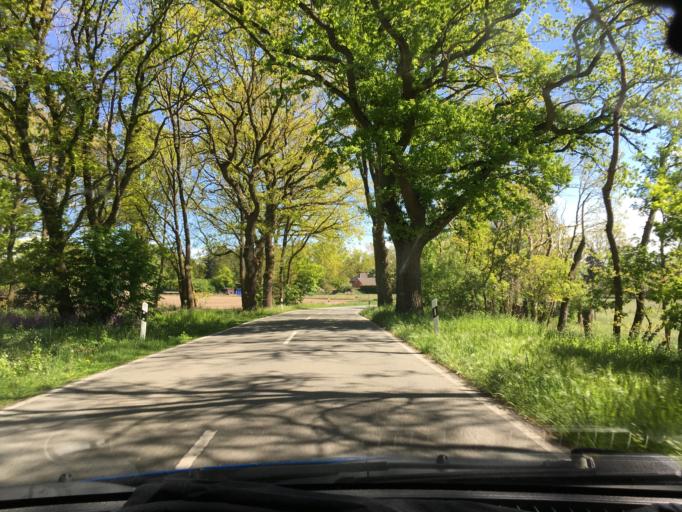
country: DE
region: Lower Saxony
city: Zernien
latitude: 53.0358
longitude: 10.8855
